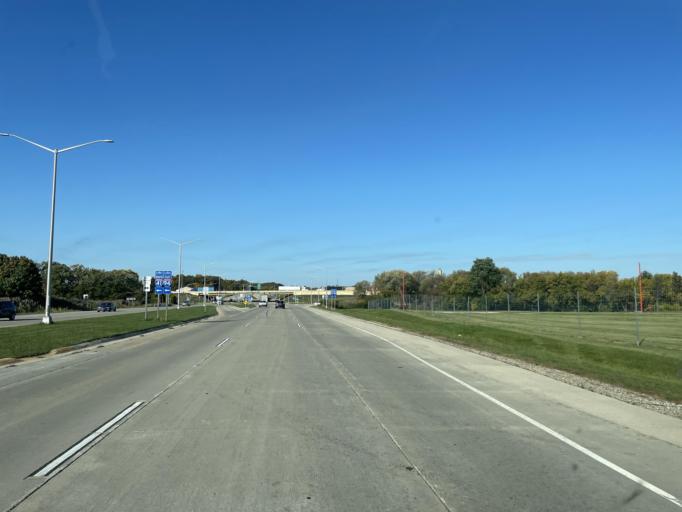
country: US
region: Wisconsin
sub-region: Kenosha County
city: Pleasant Prairie
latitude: 42.5897
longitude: -87.9480
